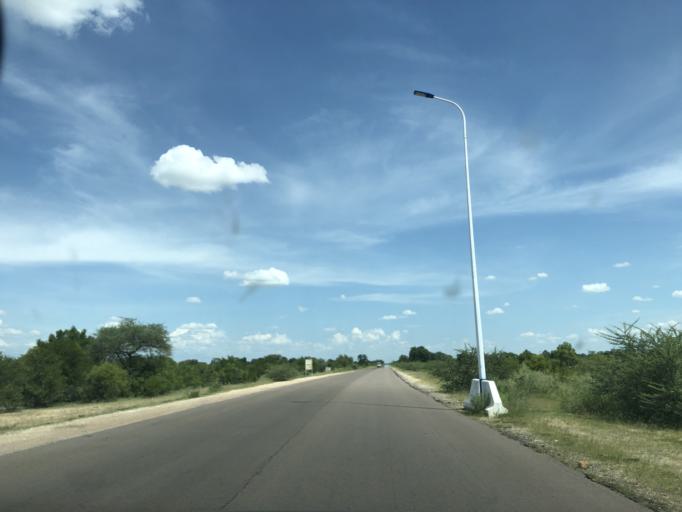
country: AO
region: Cunene
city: Ondjiva
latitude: -17.0116
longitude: 15.6497
